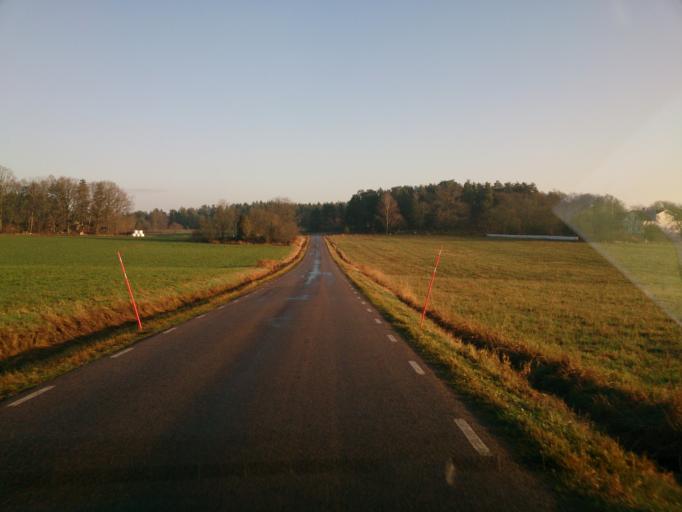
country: SE
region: OEstergoetland
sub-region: Atvidabergs Kommun
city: Atvidaberg
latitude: 58.3306
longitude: 15.9582
